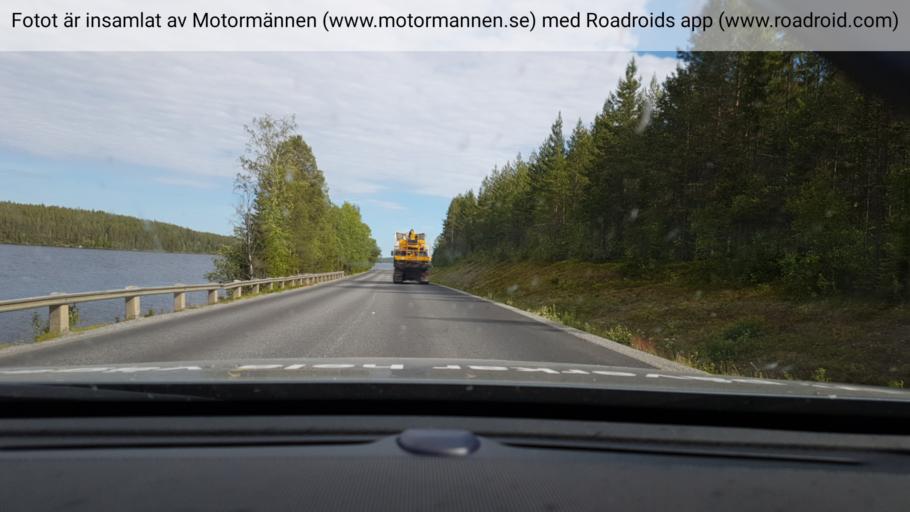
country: SE
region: Vaesterbotten
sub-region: Lycksele Kommun
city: Soderfors
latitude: 64.8501
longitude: 17.9551
